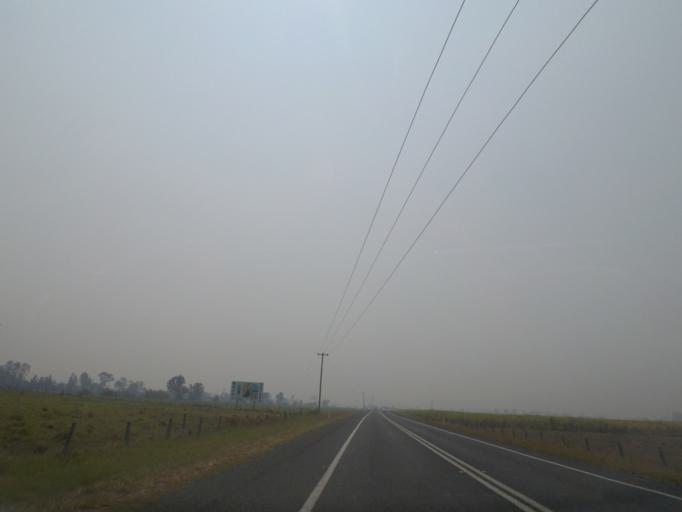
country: AU
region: New South Wales
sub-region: Clarence Valley
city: Maclean
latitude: -29.5645
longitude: 153.1077
